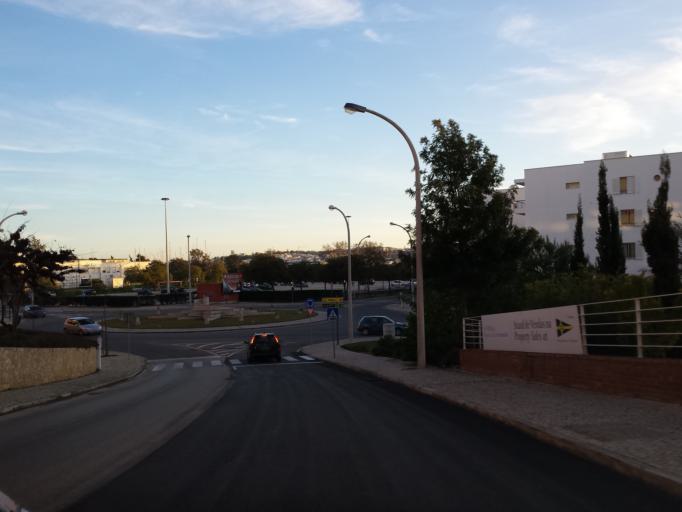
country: PT
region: Faro
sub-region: Lagos
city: Lagos
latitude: 37.1121
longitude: -8.6721
